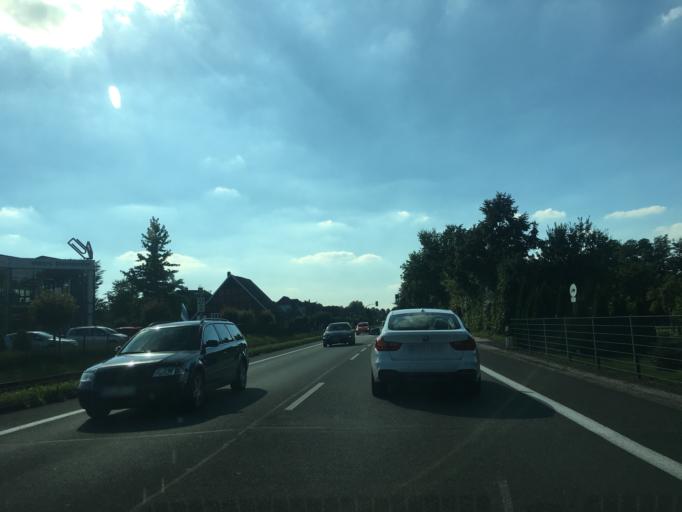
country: DE
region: North Rhine-Westphalia
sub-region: Regierungsbezirk Munster
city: Warendorf
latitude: 51.9495
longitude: 8.0081
